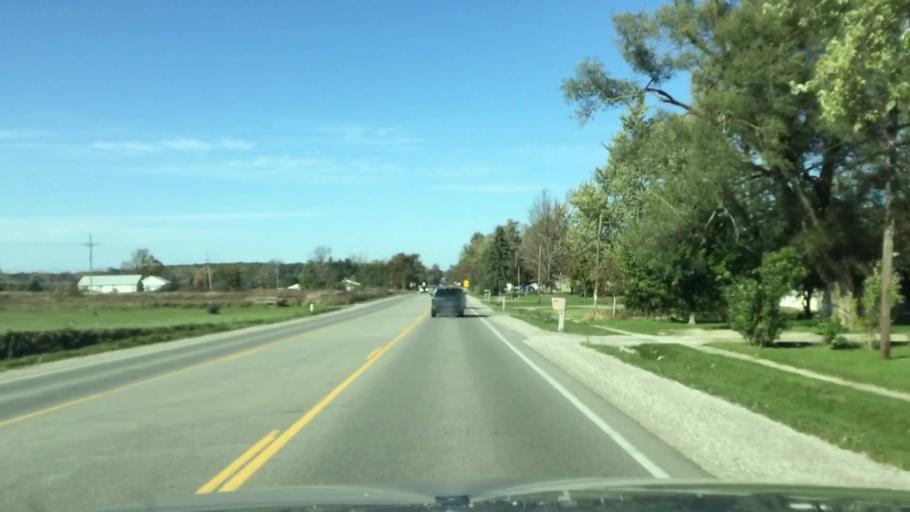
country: US
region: Michigan
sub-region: Lapeer County
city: Lapeer
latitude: 43.0615
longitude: -83.3431
